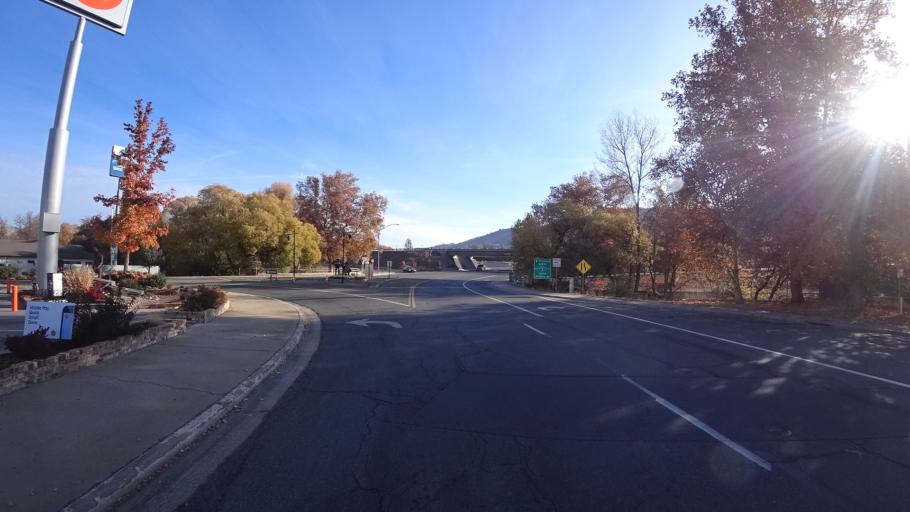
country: US
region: California
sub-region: Siskiyou County
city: Yreka
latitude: 41.7307
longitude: -122.6346
